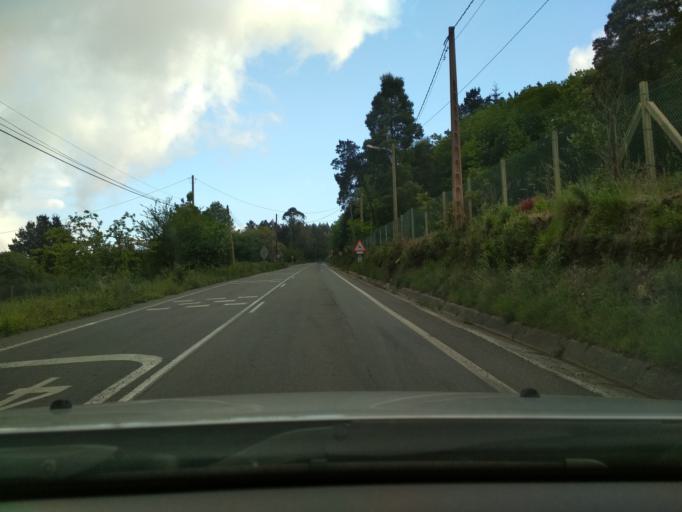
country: ES
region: Galicia
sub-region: Provincia da Coruna
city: Carballo
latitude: 43.1001
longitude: -8.6837
